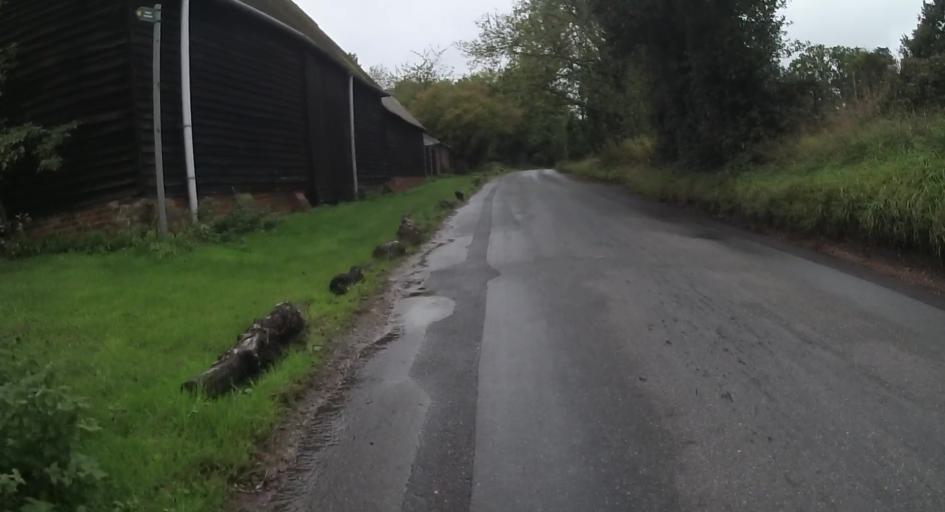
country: GB
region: England
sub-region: Hampshire
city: Tadley
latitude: 51.4129
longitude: -1.1784
